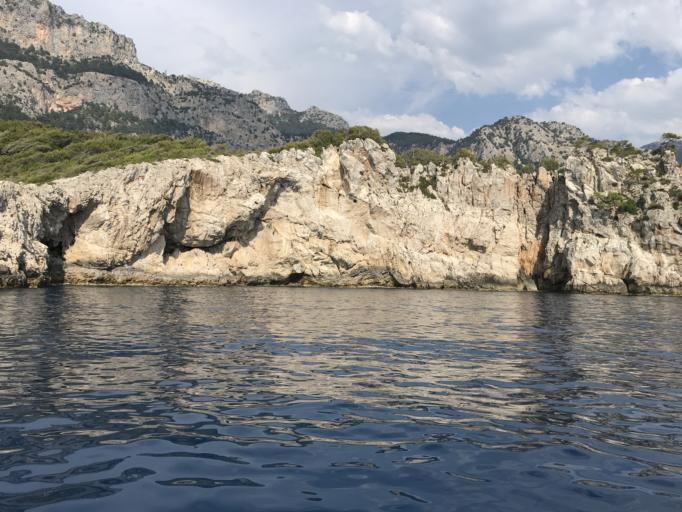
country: TR
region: Mugla
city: OEluedeniz
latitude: 36.4444
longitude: 29.1209
